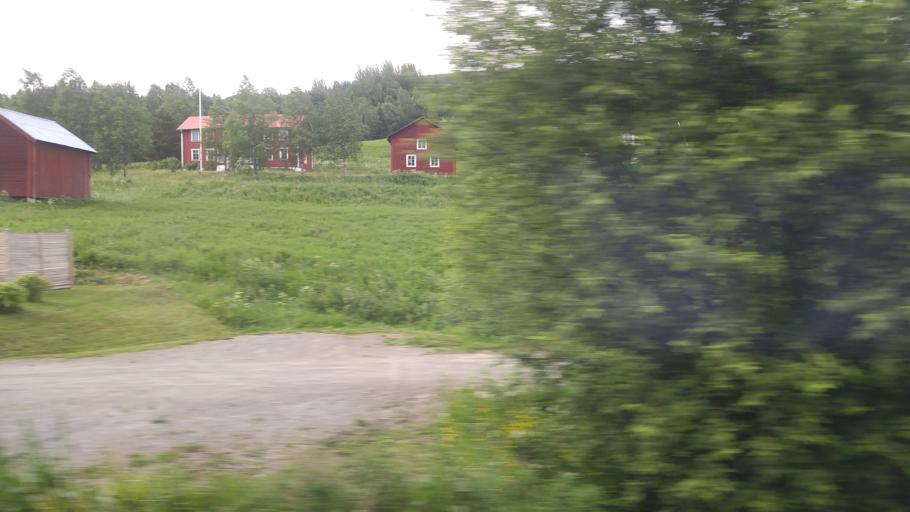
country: SE
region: Jaemtland
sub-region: Are Kommun
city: Are
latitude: 63.3930
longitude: 12.9435
